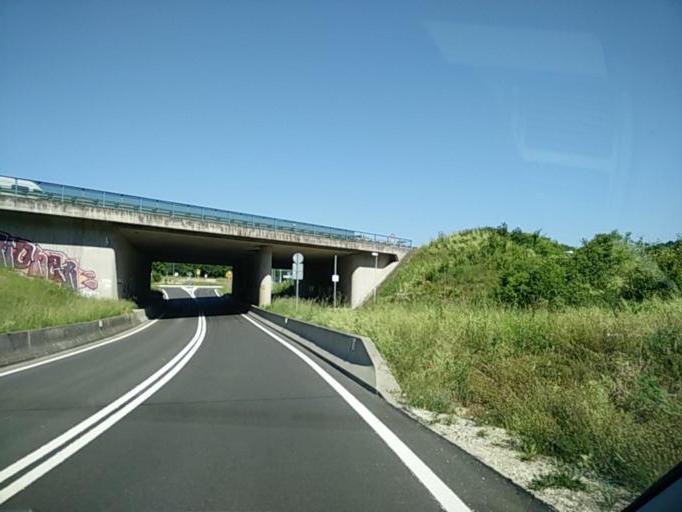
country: DE
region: Baden-Wuerttemberg
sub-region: Tuebingen Region
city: Dusslingen
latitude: 48.4869
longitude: 9.0698
